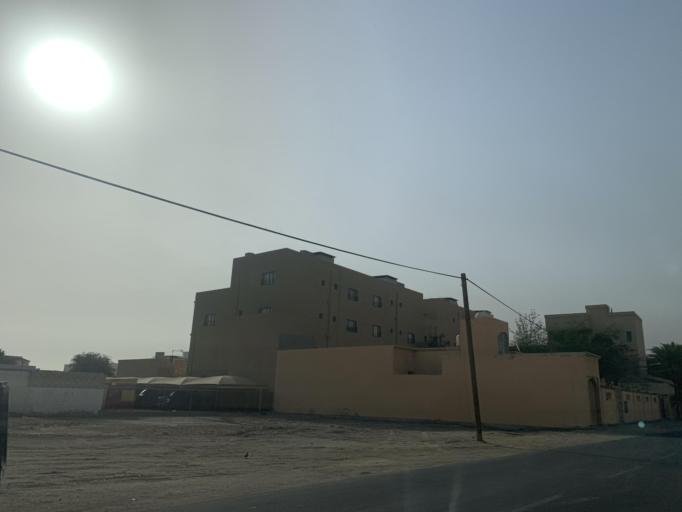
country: BH
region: Northern
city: Madinat `Isa
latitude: 26.1899
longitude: 50.5575
